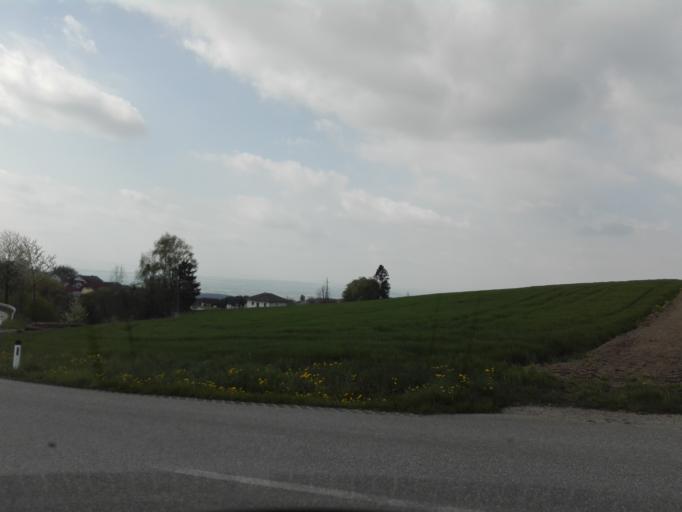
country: AT
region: Upper Austria
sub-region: Politischer Bezirk Perg
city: Perg
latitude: 48.2864
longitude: 14.6805
